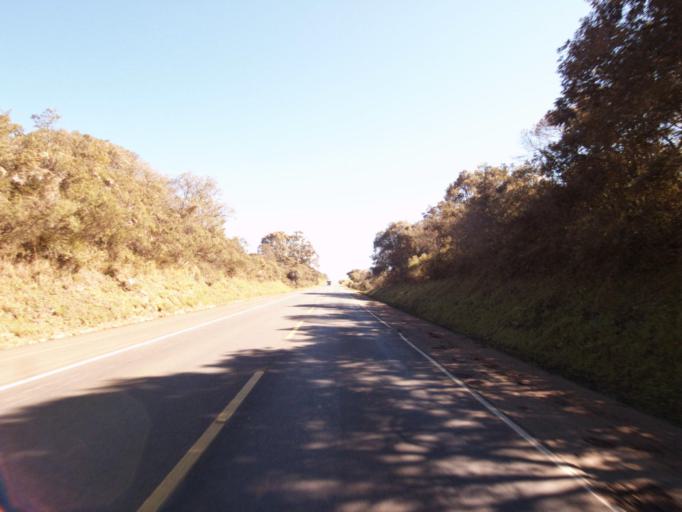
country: BR
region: Santa Catarina
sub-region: Xanxere
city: Xanxere
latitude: -26.8648
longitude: -52.2131
